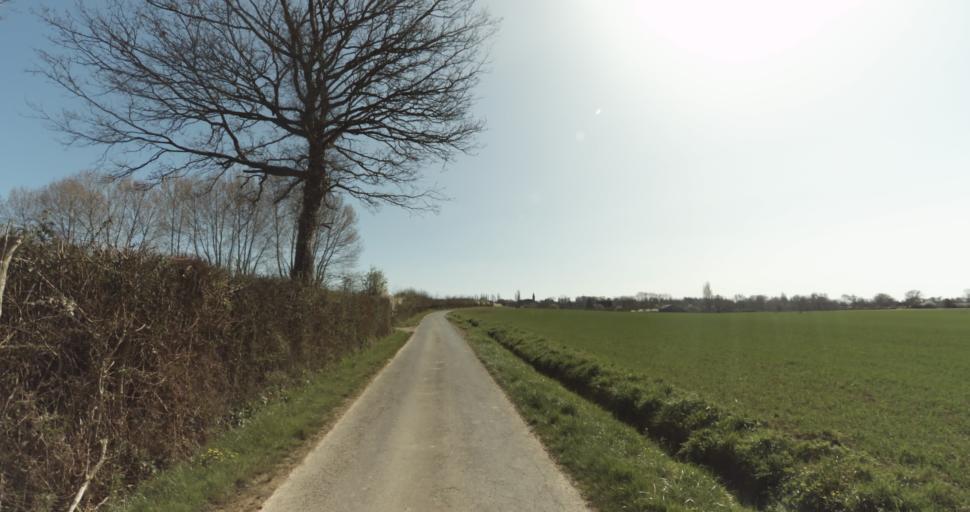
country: FR
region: Lower Normandy
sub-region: Departement du Calvados
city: Saint-Pierre-sur-Dives
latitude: 48.9509
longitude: -0.0041
